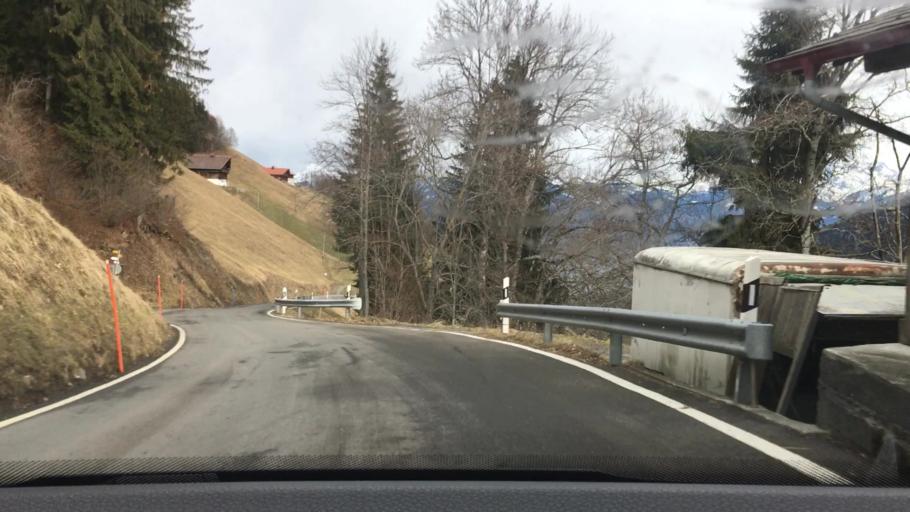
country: CH
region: Valais
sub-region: Monthey District
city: Troistorrents
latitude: 46.2095
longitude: 6.8881
